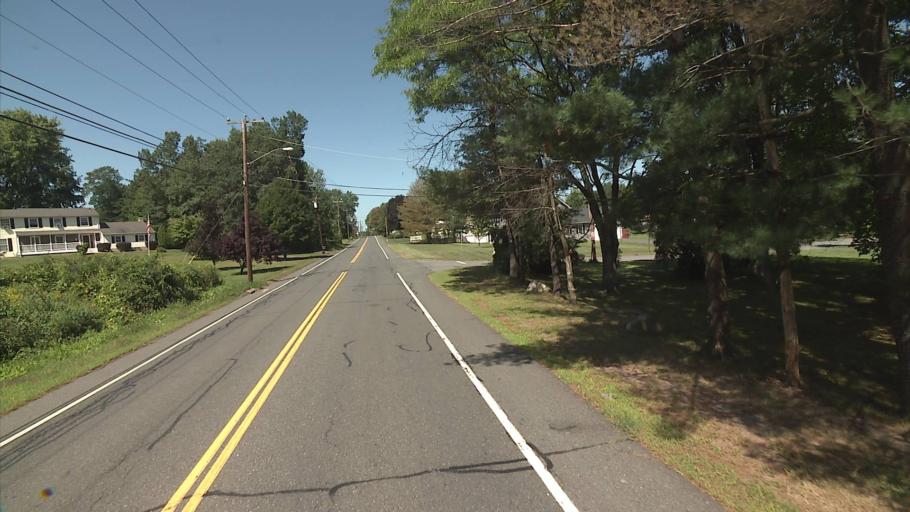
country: US
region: Connecticut
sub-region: Hartford County
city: Thompsonville
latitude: 42.0160
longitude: -72.6165
